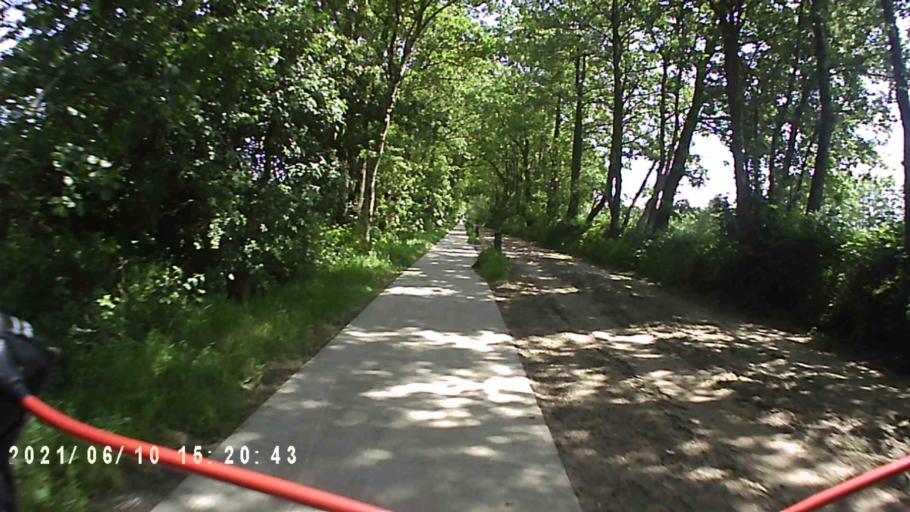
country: NL
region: Friesland
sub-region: Gemeente Achtkarspelen
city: Surhuisterveen
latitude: 53.1916
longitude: 6.1779
